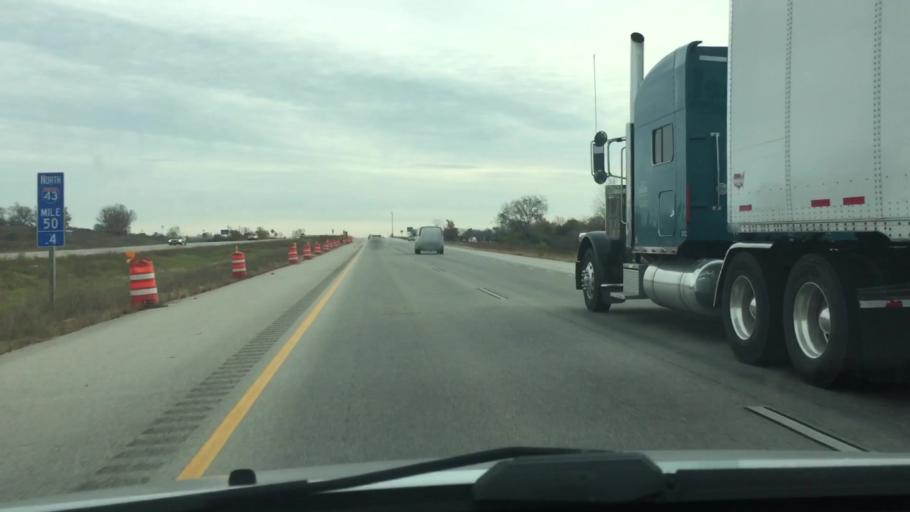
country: US
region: Wisconsin
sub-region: Waukesha County
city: Big Bend
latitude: 42.9095
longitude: -88.2227
